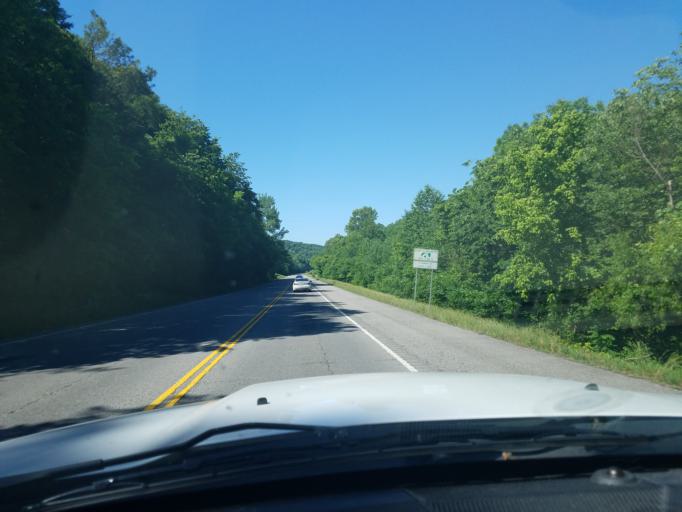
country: US
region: Tennessee
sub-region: Sumner County
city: Westmoreland
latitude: 36.5343
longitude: -86.2459
